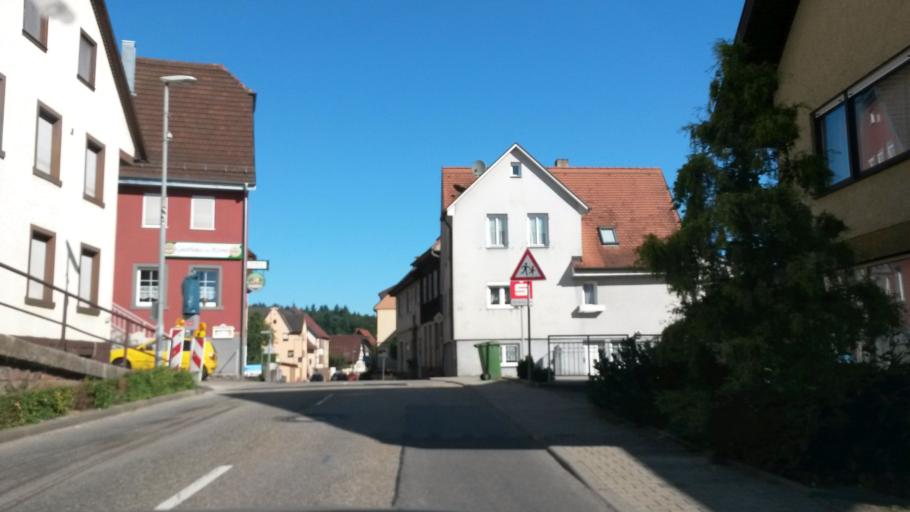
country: DE
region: Baden-Wuerttemberg
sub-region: Karlsruhe Region
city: Konigsbach-Stein
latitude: 48.9481
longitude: 8.6217
